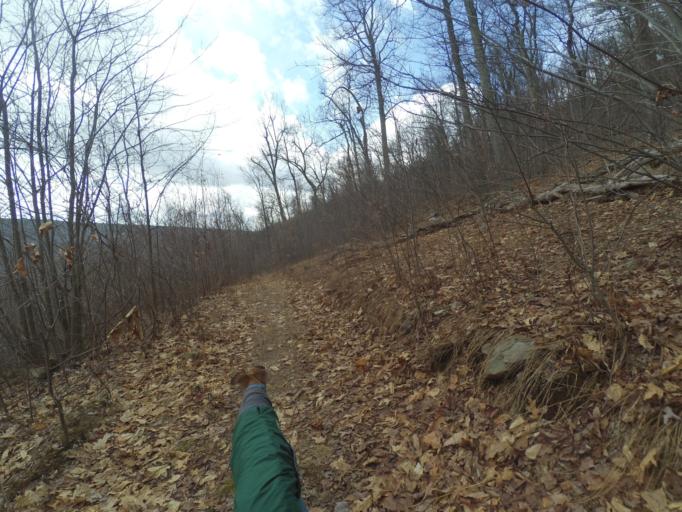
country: US
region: Pennsylvania
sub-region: Centre County
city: Boalsburg
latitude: 40.7613
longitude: -77.7147
